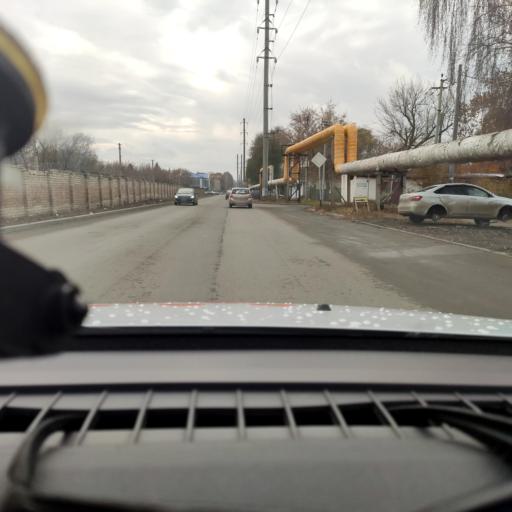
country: RU
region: Samara
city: Chapayevsk
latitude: 52.9812
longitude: 49.7213
